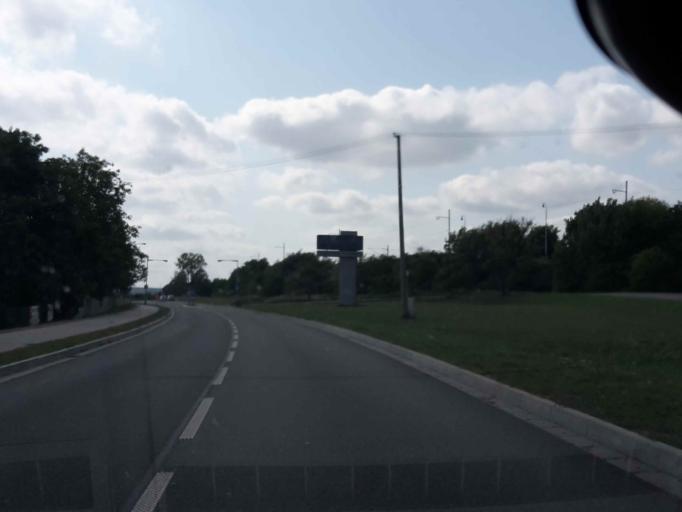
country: CZ
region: South Moravian
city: Rousinov
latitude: 49.2172
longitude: 16.9013
